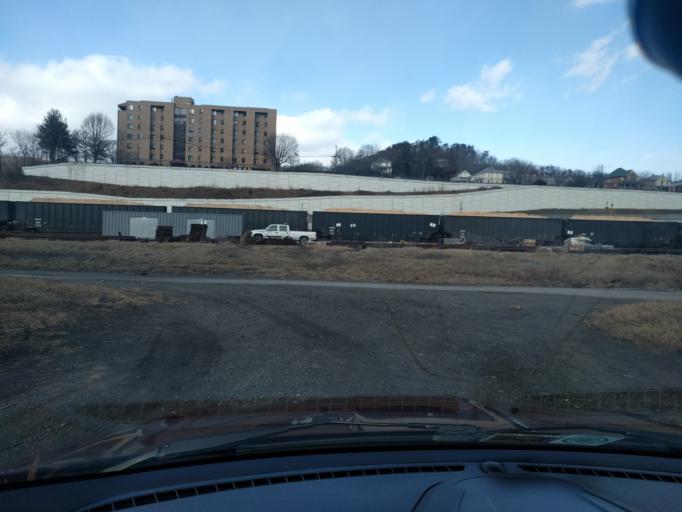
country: US
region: Virginia
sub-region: Alleghany County
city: Clifton Forge
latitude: 37.8089
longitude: -79.8412
